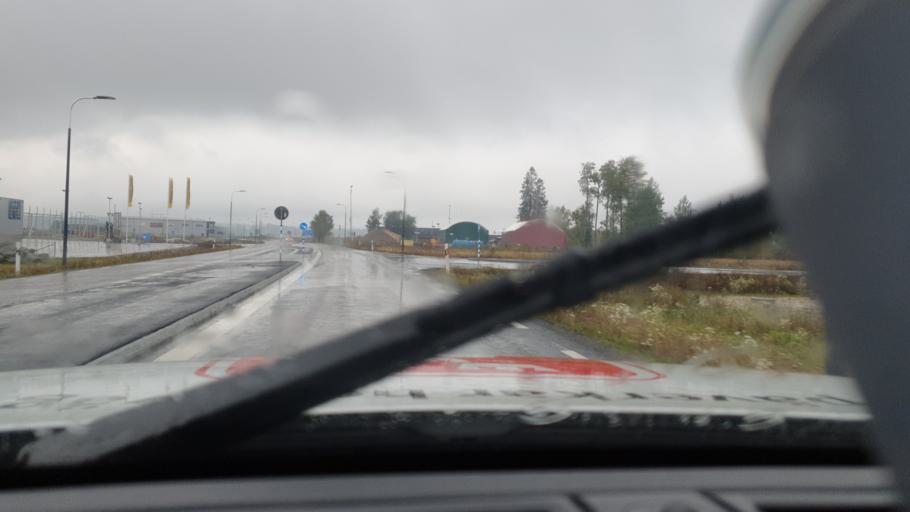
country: SE
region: Uppsala
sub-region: Tierps Kommun
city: Tierp
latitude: 60.3441
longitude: 17.4956
